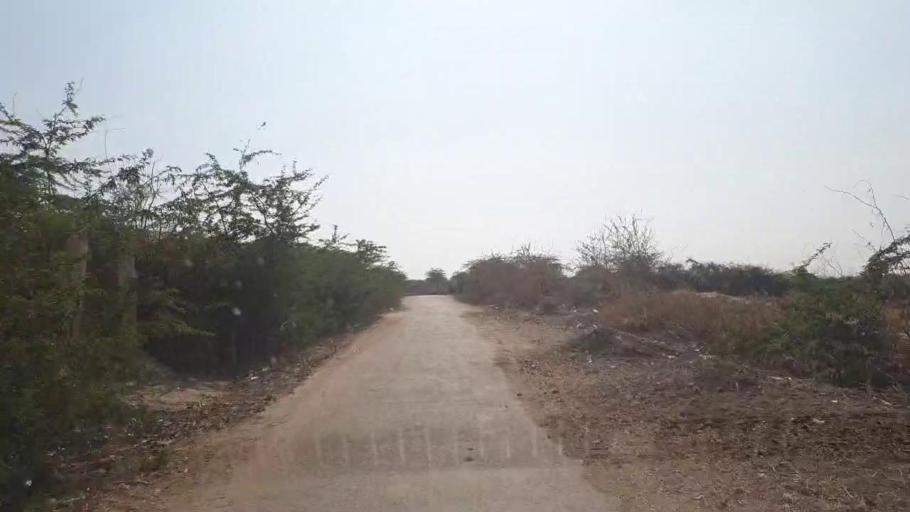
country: PK
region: Sindh
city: Dhoro Naro
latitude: 25.4989
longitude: 69.6292
